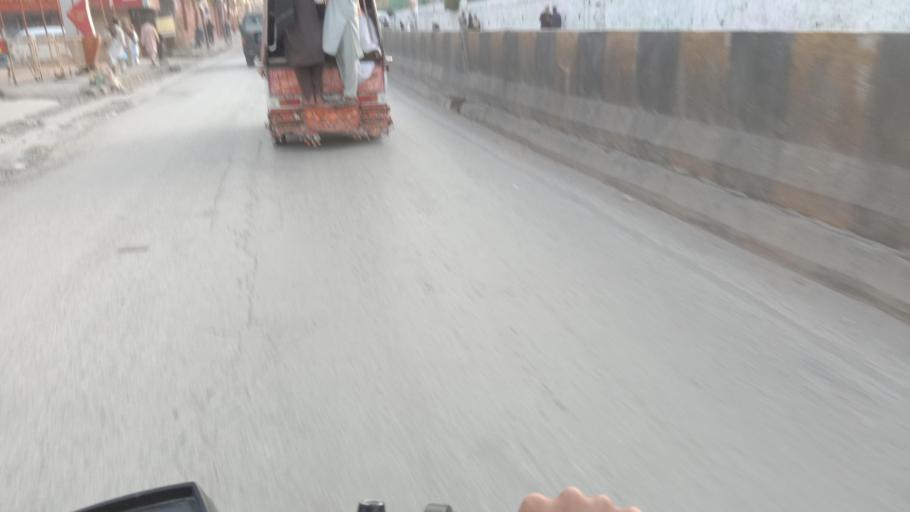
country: PK
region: Khyber Pakhtunkhwa
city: Abbottabad
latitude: 34.1438
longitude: 73.2146
